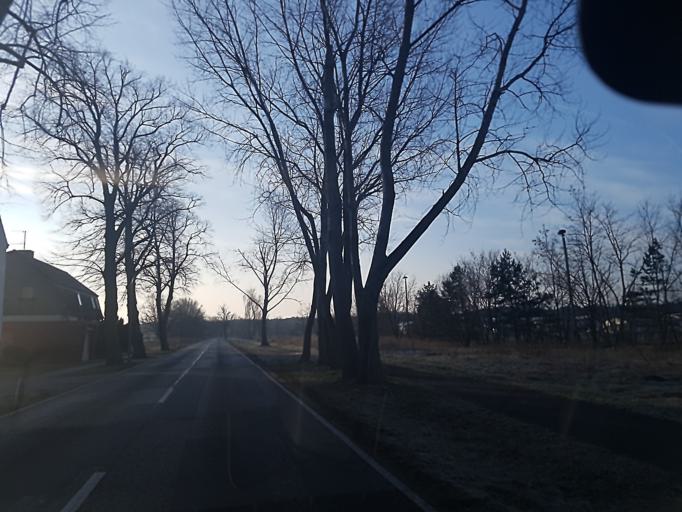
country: DE
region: Brandenburg
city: Golzow
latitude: 52.2698
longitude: 12.5988
